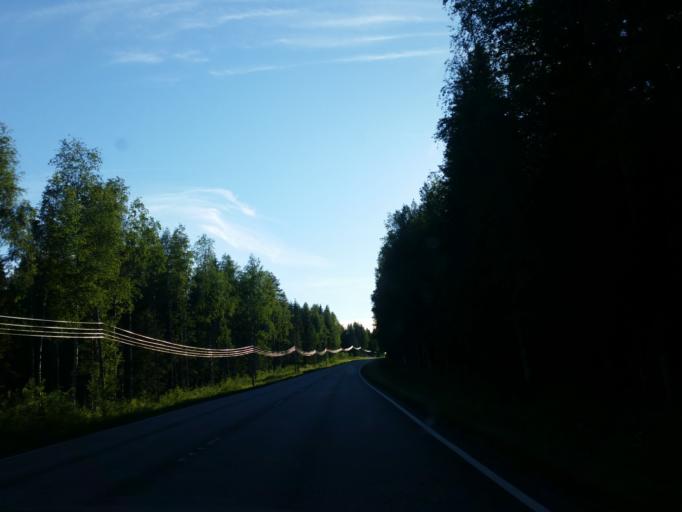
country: FI
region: Northern Savo
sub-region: Kuopio
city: Kuopio
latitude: 62.8449
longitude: 27.4105
